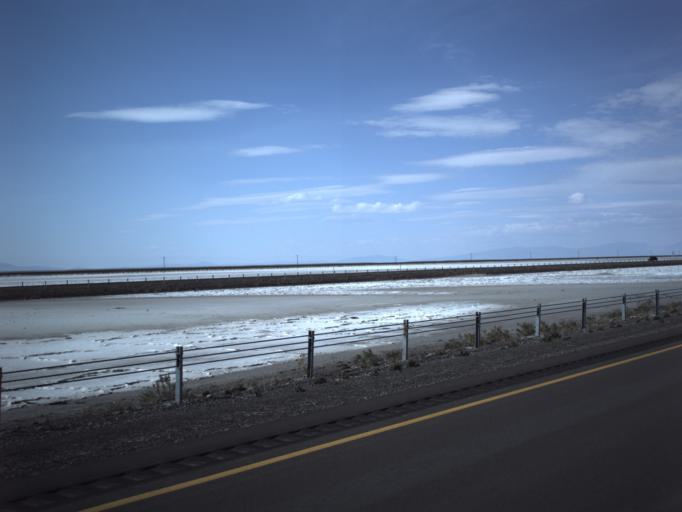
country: US
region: Utah
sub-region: Tooele County
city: Wendover
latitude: 40.7299
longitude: -113.4172
